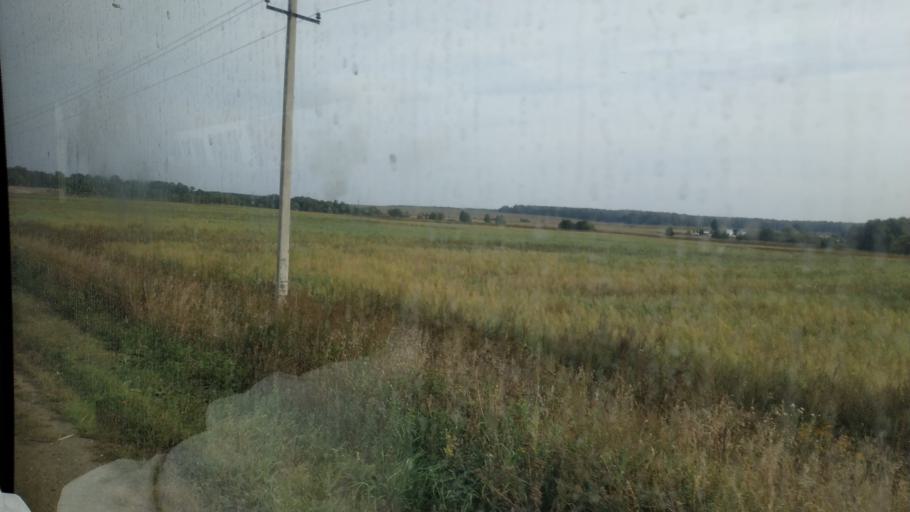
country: RU
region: Moskovskaya
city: Il'inskoye
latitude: 55.3297
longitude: 38.0703
